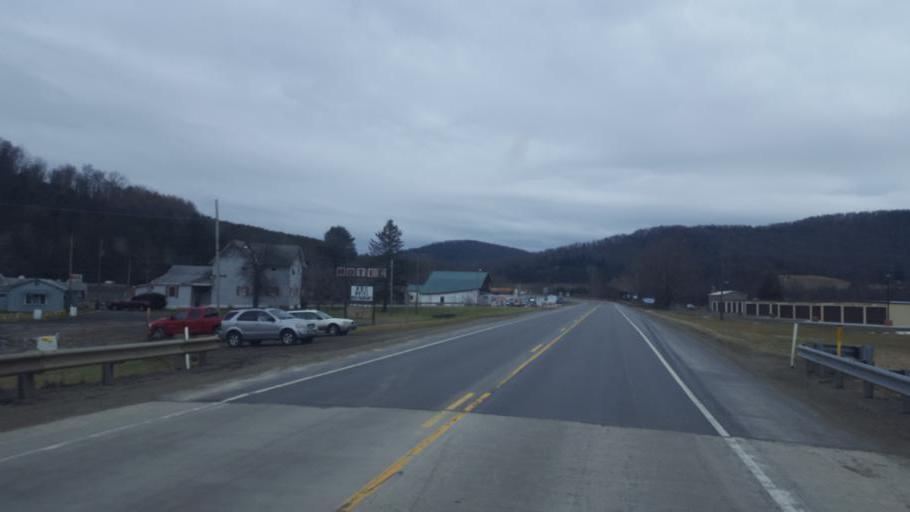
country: US
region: Pennsylvania
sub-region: McKean County
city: Port Allegany
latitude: 41.7889
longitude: -78.2066
